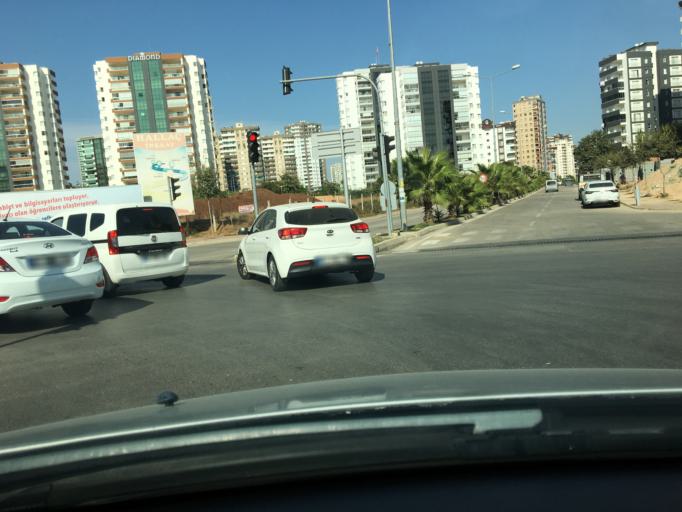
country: TR
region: Adana
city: Seyhan
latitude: 37.0224
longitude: 35.2583
